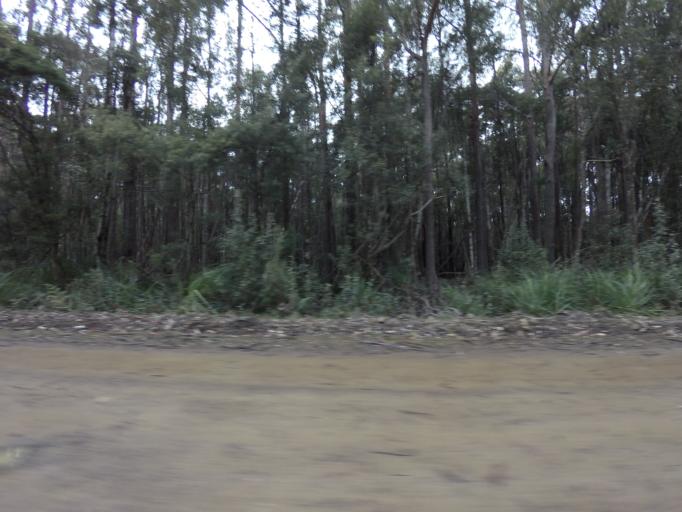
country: AU
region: Tasmania
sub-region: Huon Valley
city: Geeveston
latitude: -43.4919
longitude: 146.8877
